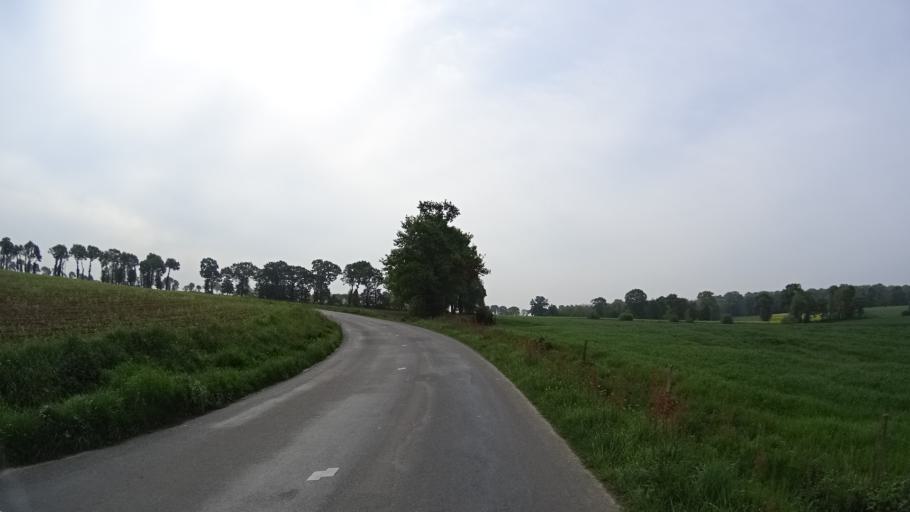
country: FR
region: Brittany
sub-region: Departement d'Ille-et-Vilaine
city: Montreuil-le-Gast
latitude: 48.2493
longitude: -1.7449
